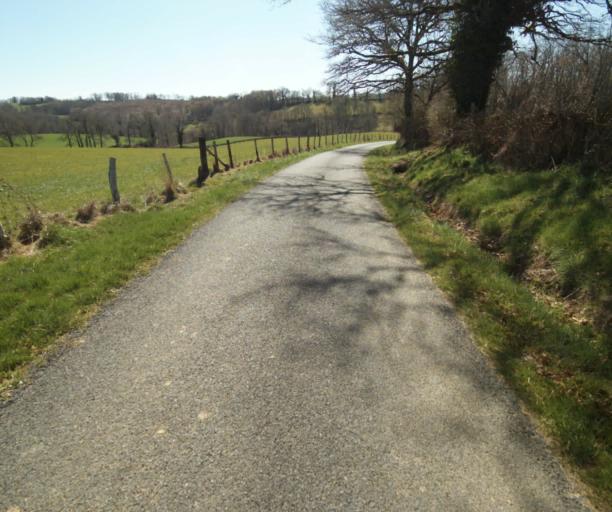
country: FR
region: Limousin
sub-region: Departement de la Correze
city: Chamboulive
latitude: 45.4570
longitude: 1.6881
